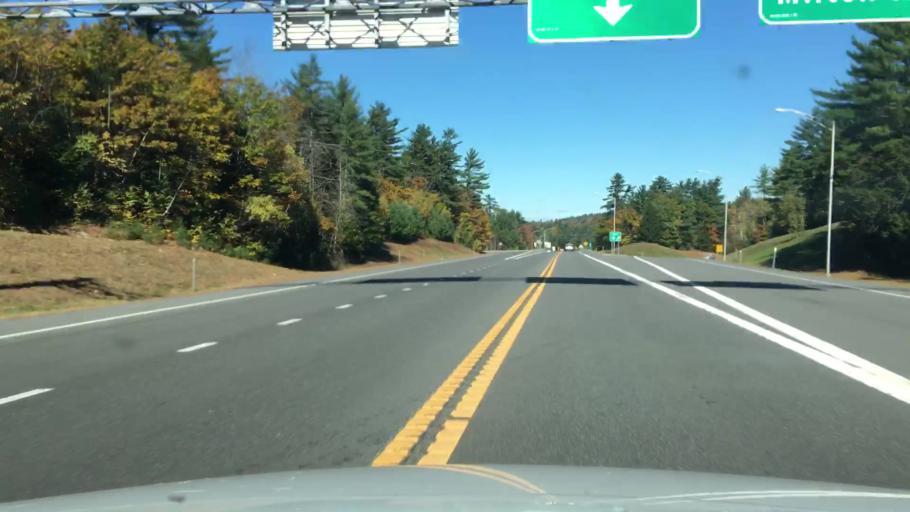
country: US
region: New Hampshire
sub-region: Carroll County
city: Sanbornville
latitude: 43.4759
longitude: -71.0029
